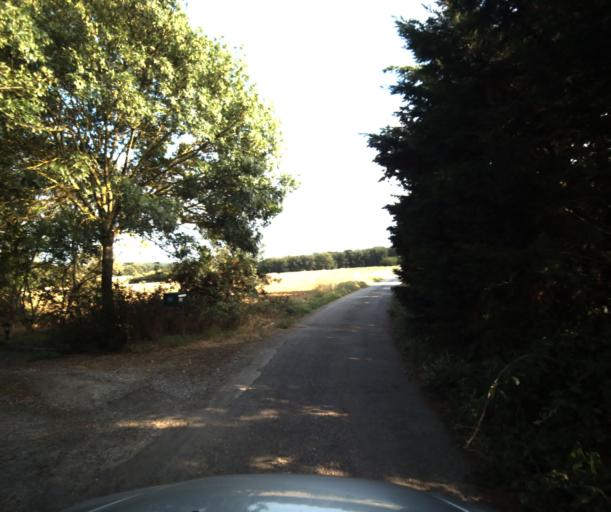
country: FR
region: Midi-Pyrenees
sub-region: Departement de la Haute-Garonne
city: Eaunes
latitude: 43.4305
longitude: 1.3342
